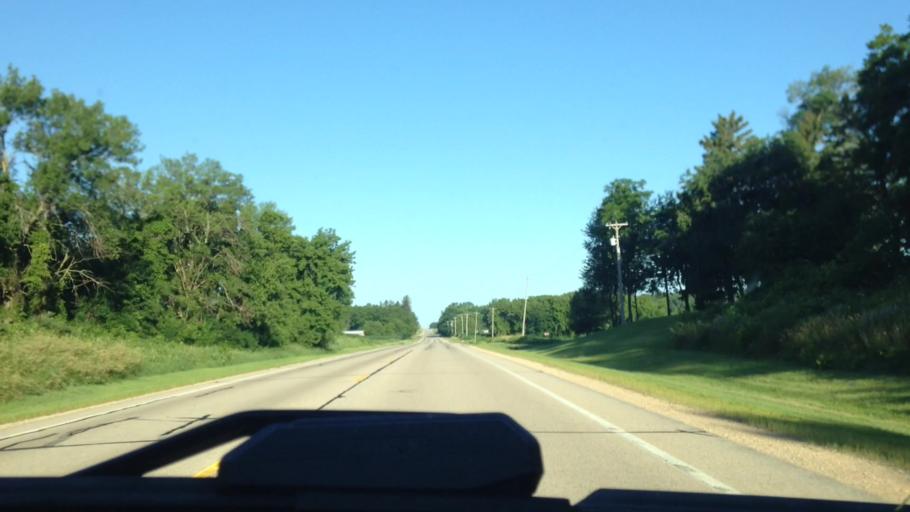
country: US
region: Wisconsin
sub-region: Dane County
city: De Forest
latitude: 43.3327
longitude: -89.2755
